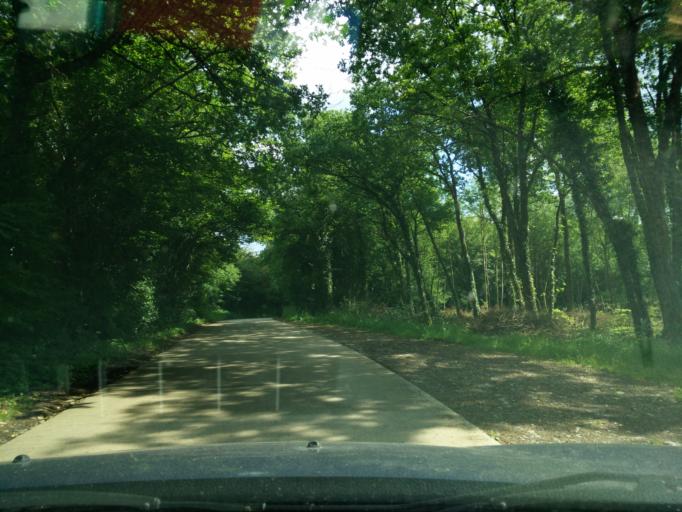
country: BE
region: Wallonia
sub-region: Province de Namur
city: Couvin
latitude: 50.0896
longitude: 4.6067
